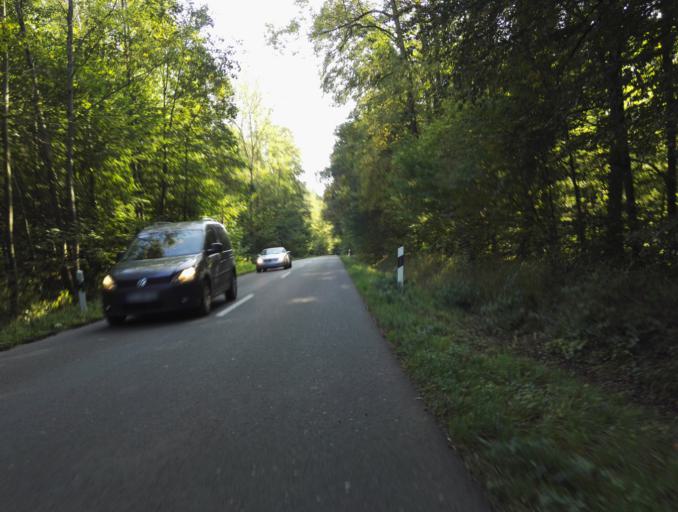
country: DE
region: Lower Saxony
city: Holle
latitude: 52.1317
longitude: 10.1396
